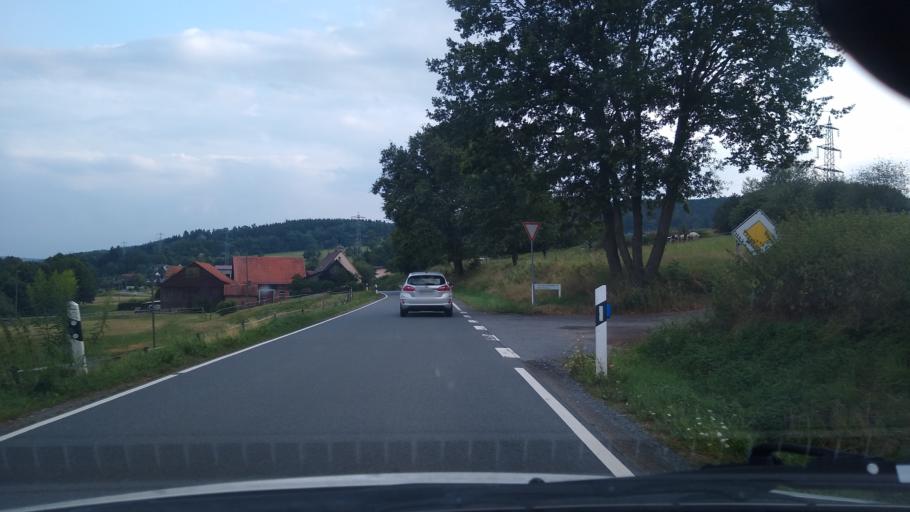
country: DE
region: Hesse
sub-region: Regierungsbezirk Darmstadt
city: Erbach
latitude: 49.6806
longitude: 8.9226
